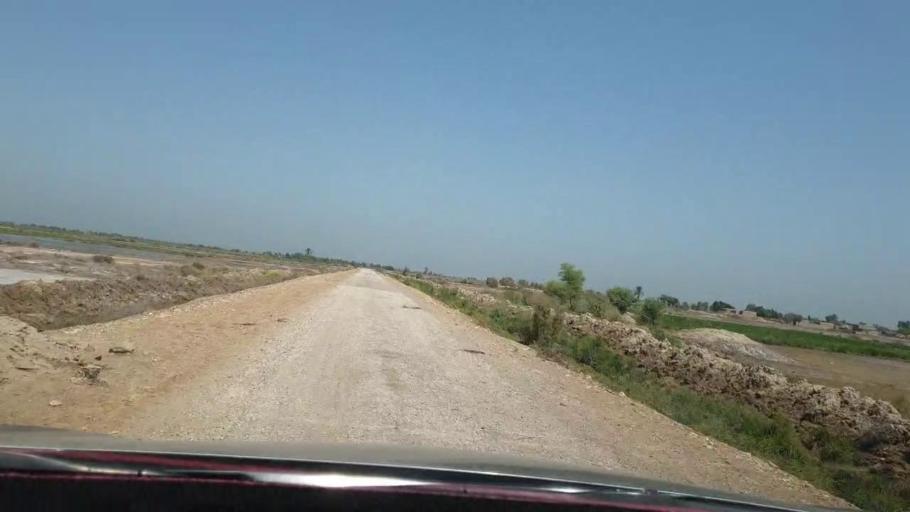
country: PK
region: Sindh
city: Warah
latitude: 27.5321
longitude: 67.7221
